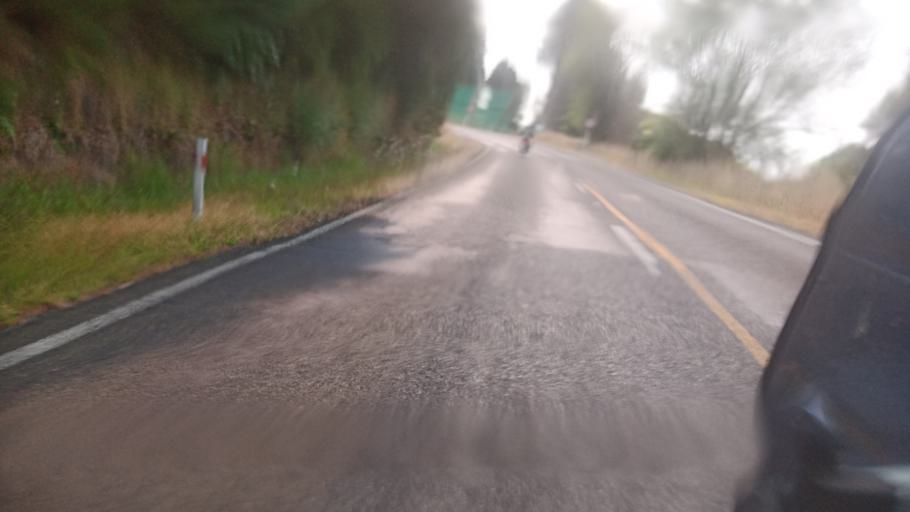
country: NZ
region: Bay of Plenty
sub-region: Opotiki District
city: Opotiki
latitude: -37.9449
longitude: 177.4982
